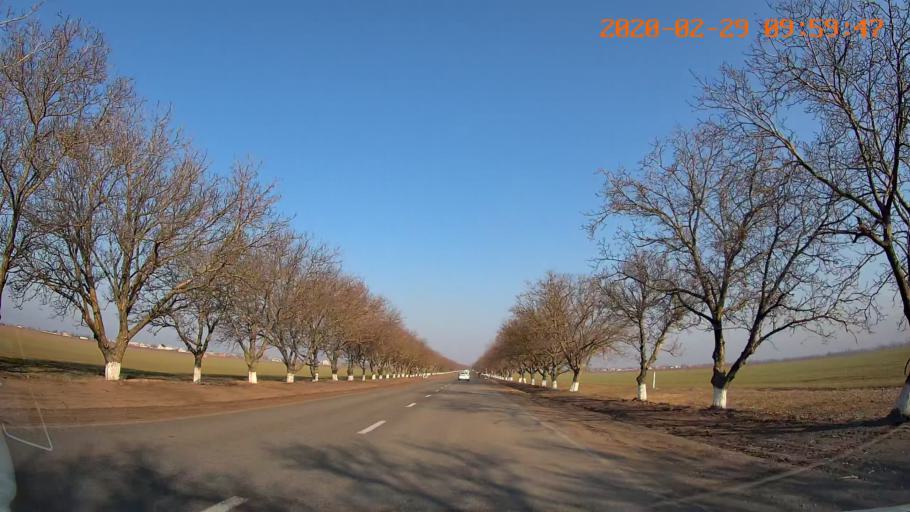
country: MD
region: Telenesti
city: Slobozia
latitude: 46.7607
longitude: 29.6877
